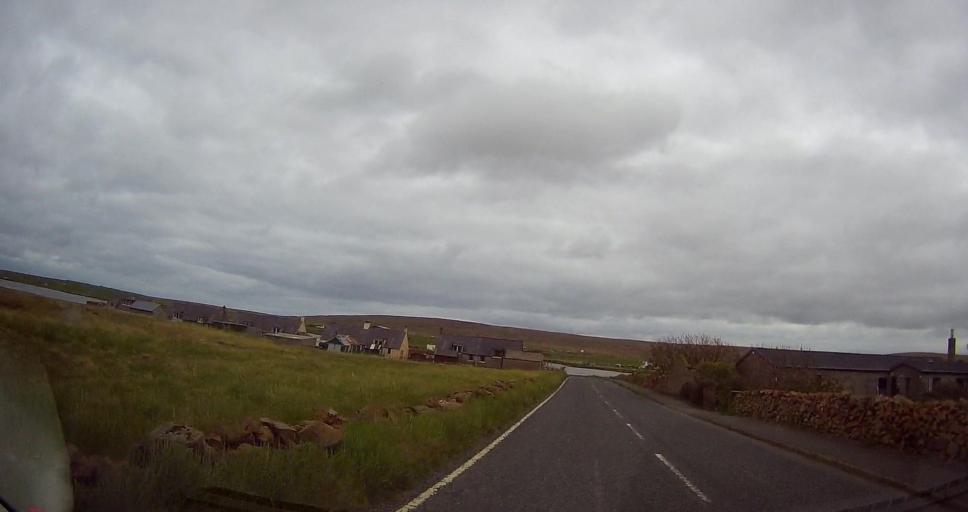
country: GB
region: Scotland
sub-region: Shetland Islands
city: Shetland
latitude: 60.7599
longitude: -0.8588
